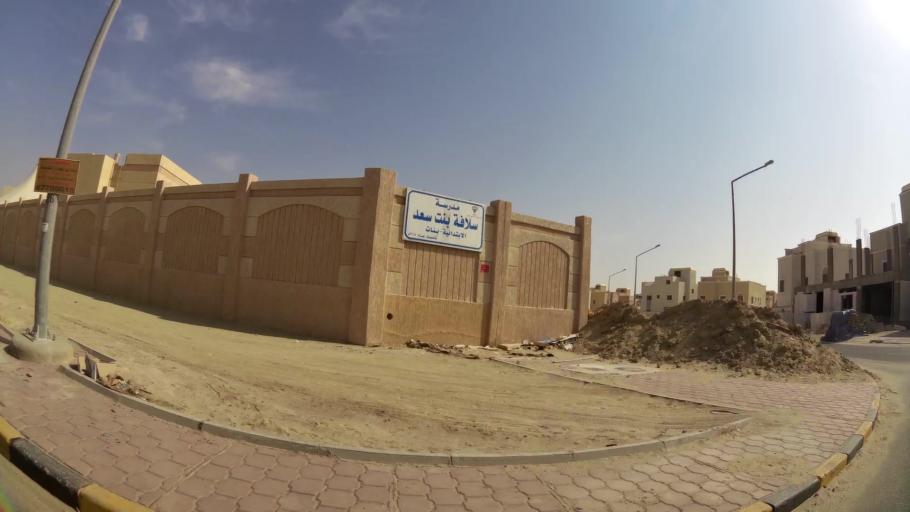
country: KW
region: Al Ahmadi
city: Al Wafrah
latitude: 28.7907
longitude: 48.0717
